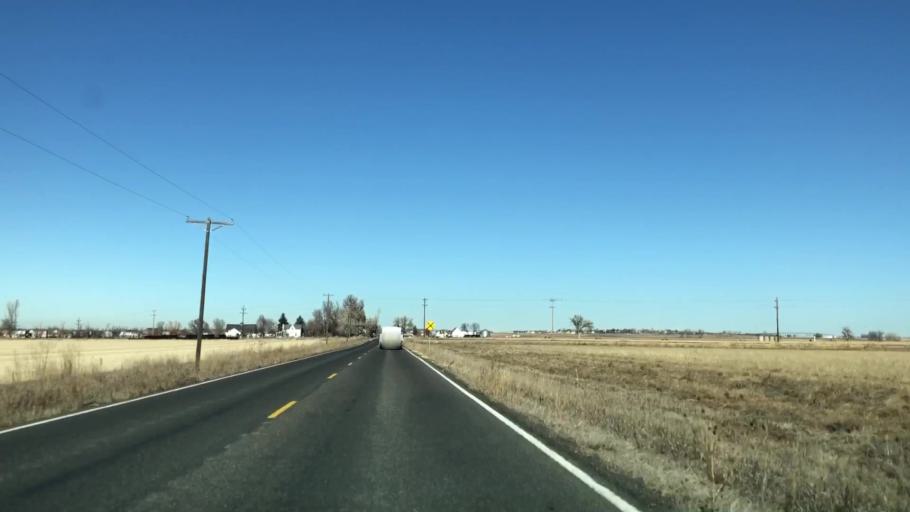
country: US
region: Colorado
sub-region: Weld County
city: Windsor
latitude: 40.5024
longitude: -104.9441
